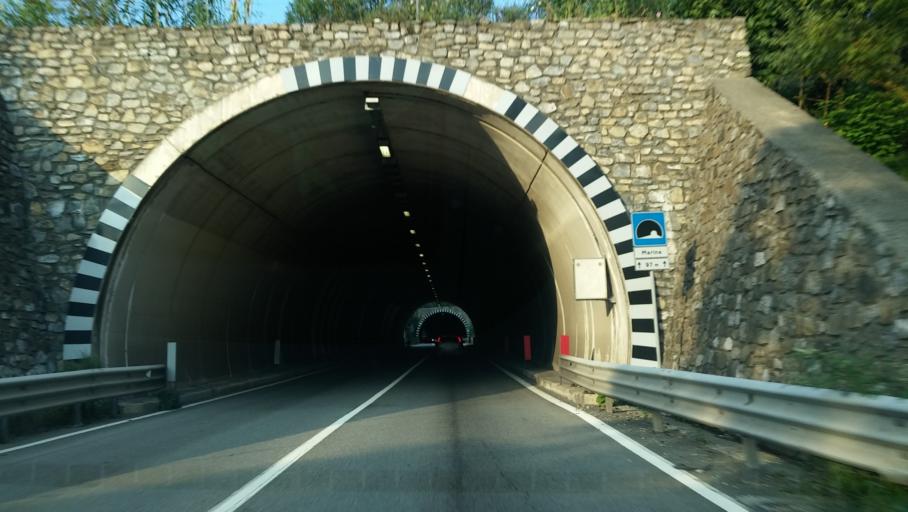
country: IT
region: Lombardy
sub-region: Provincia di Lecco
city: Lecco
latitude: 45.8640
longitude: 9.4180
